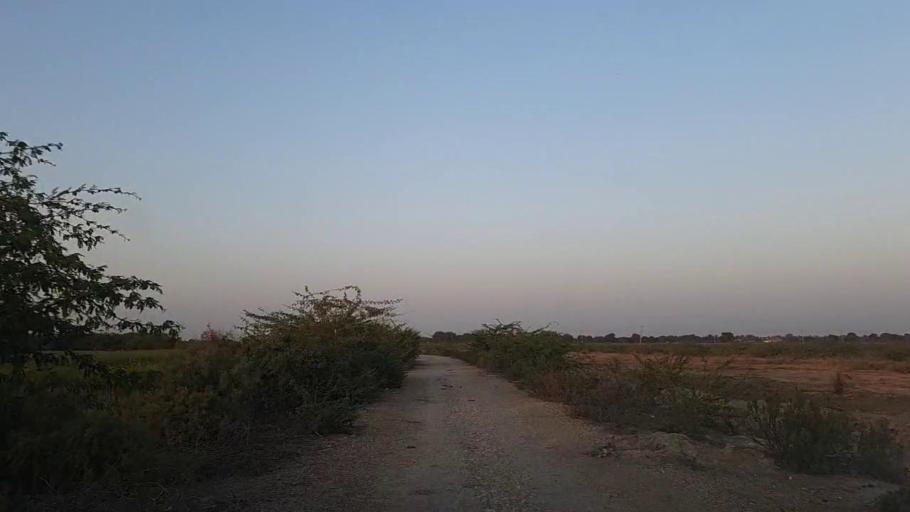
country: PK
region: Sindh
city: Naukot
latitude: 24.8804
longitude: 69.3531
